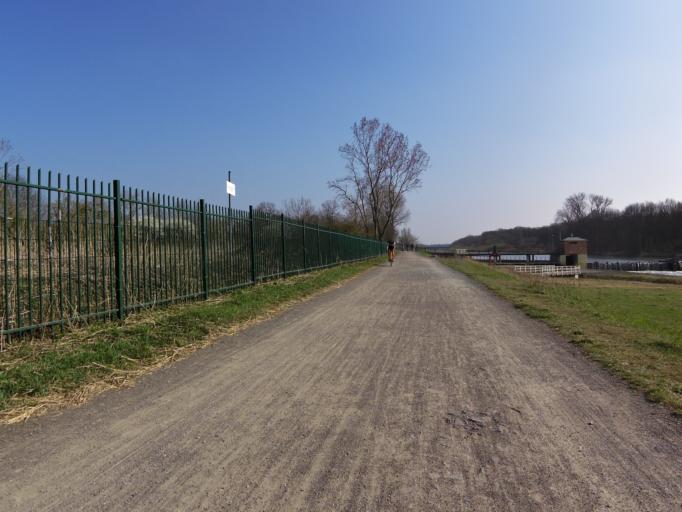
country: DE
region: Saxony
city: Leipzig
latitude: 51.3588
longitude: 12.3362
